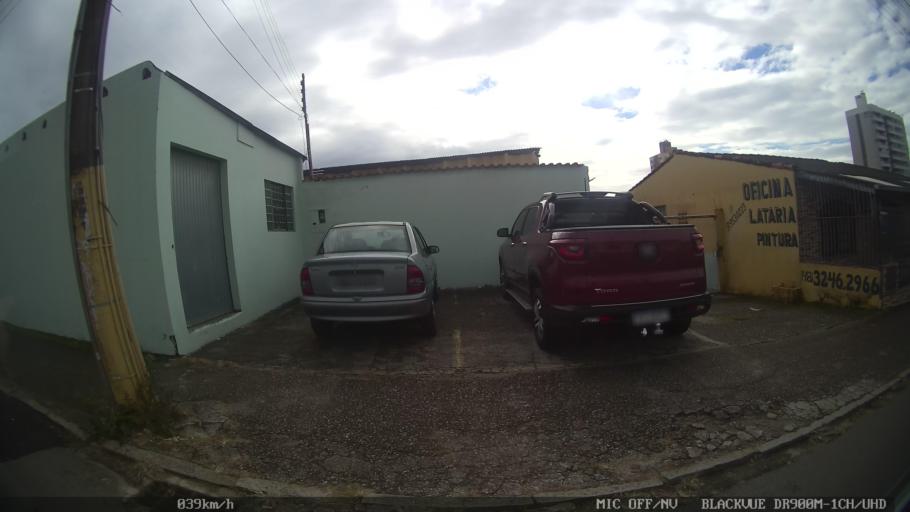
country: BR
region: Santa Catarina
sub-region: Sao Jose
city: Campinas
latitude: -27.5734
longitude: -48.6125
